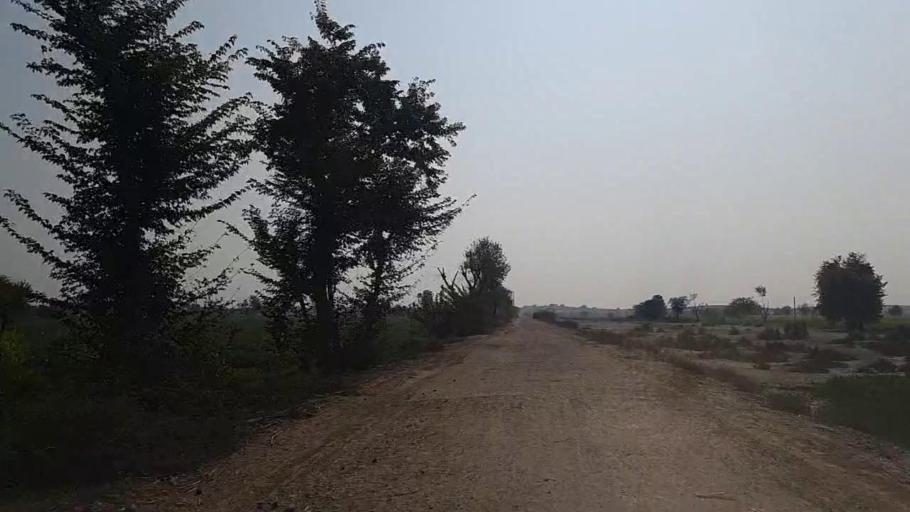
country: PK
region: Sindh
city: Jam Sahib
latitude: 26.4531
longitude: 68.5234
